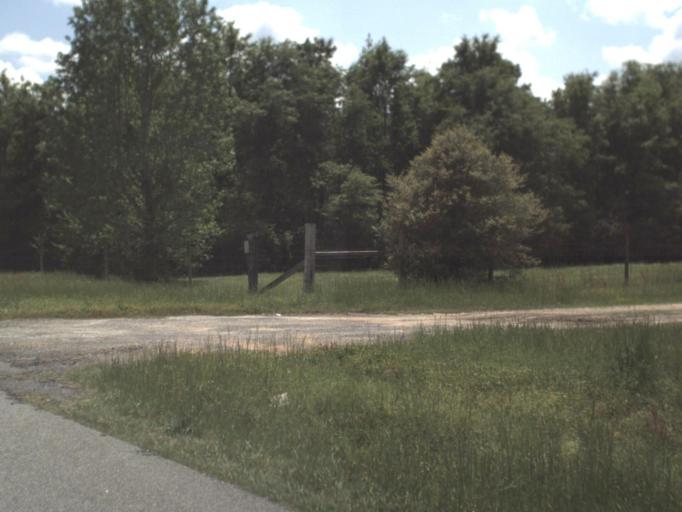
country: US
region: Florida
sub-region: Escambia County
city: Molino
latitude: 30.8108
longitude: -87.4262
